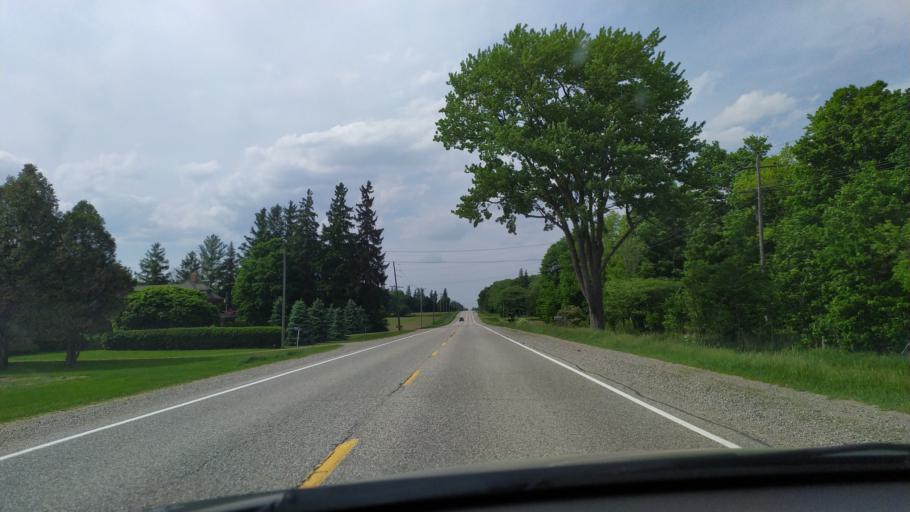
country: CA
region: Ontario
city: Dorchester
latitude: 43.0932
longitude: -81.0067
